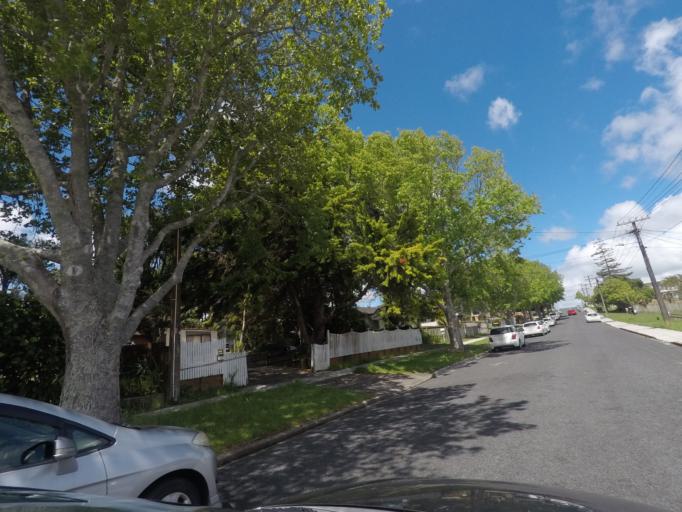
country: NZ
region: Auckland
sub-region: Auckland
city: Rosebank
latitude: -36.8810
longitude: 174.6444
